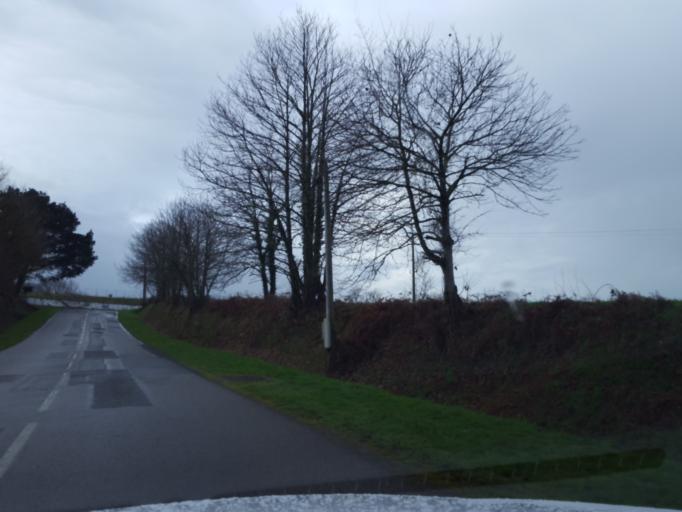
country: FR
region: Brittany
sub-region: Departement d'Ille-et-Vilaine
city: Guignen
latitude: 47.9150
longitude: -1.8610
